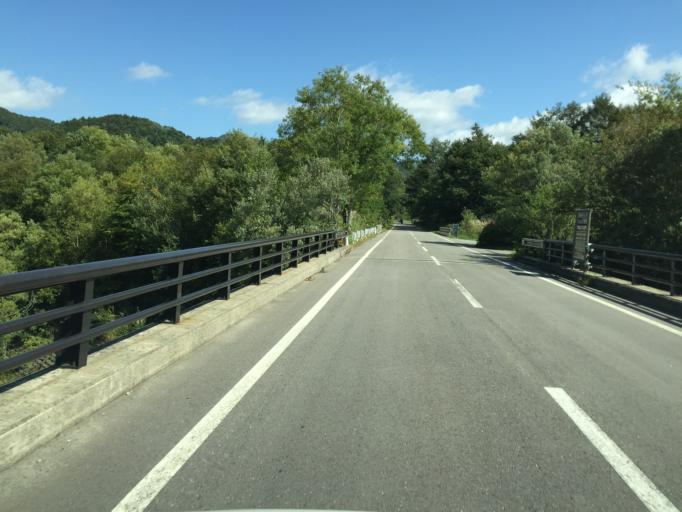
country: JP
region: Fukushima
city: Inawashiro
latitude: 37.6547
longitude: 140.1894
